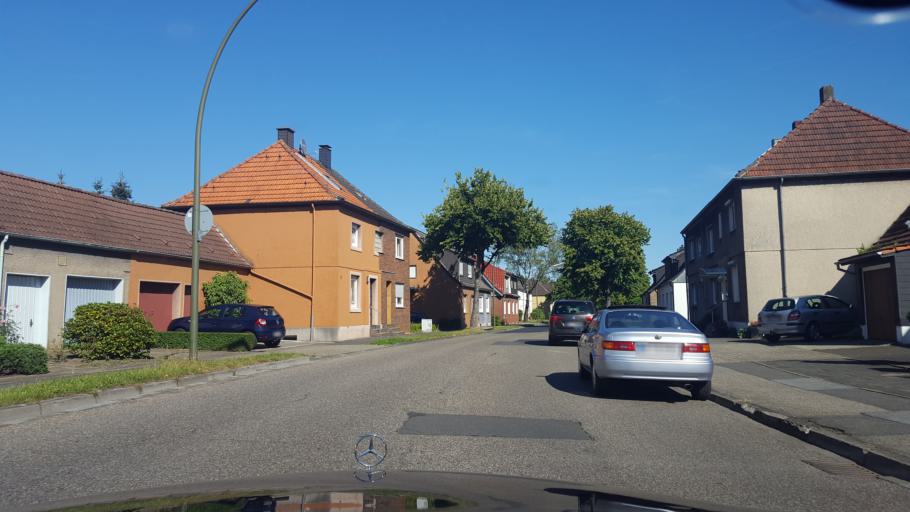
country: DE
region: North Rhine-Westphalia
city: Marl
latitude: 51.6688
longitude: 7.1180
